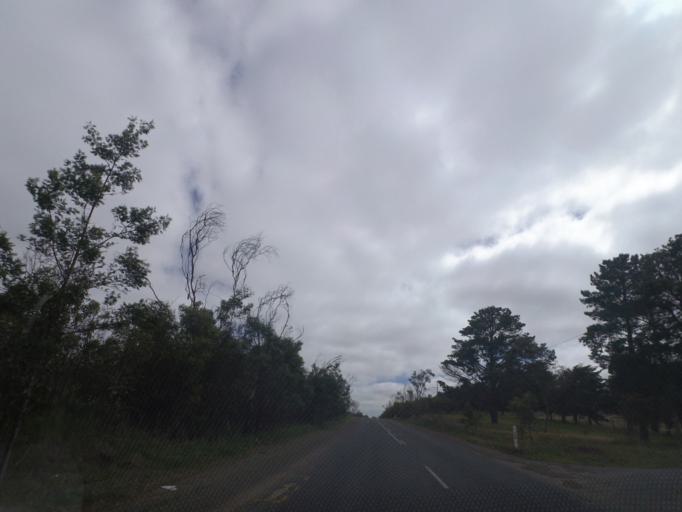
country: AU
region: Victoria
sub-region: Hume
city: Craigieburn
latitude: -37.5186
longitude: 144.8940
